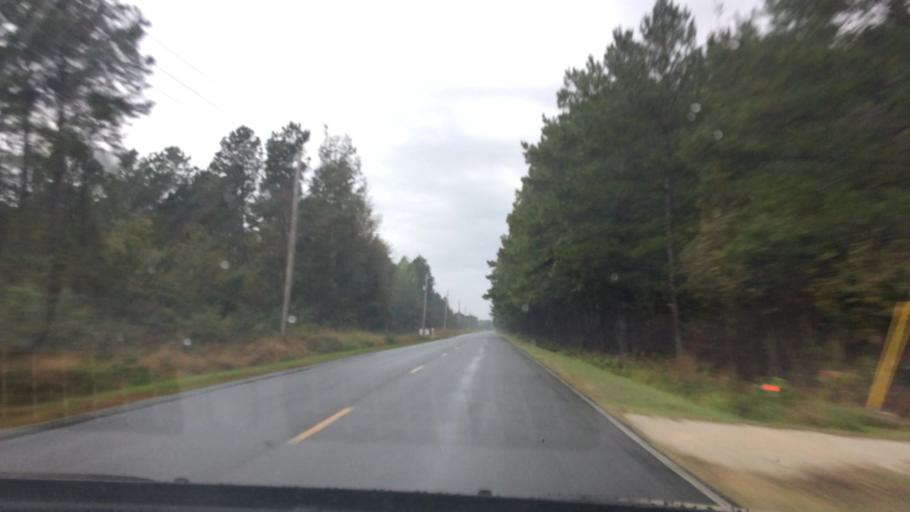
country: US
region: North Carolina
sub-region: Pitt County
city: Grifton
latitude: 35.3978
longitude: -77.4018
